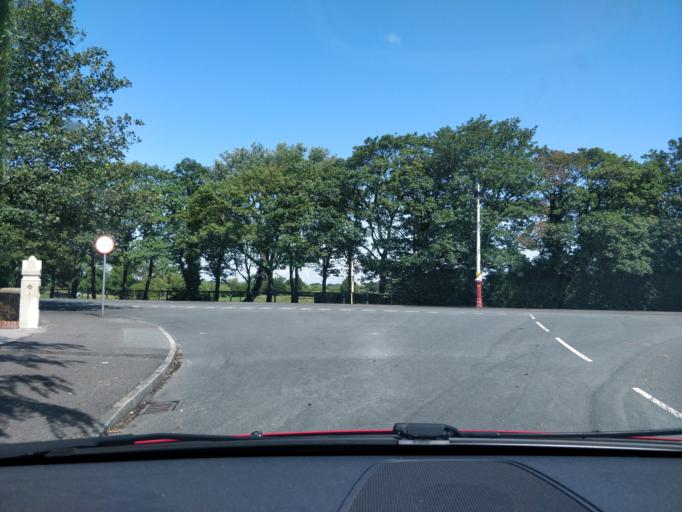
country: GB
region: England
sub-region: Sefton
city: Southport
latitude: 53.6581
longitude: -2.9957
